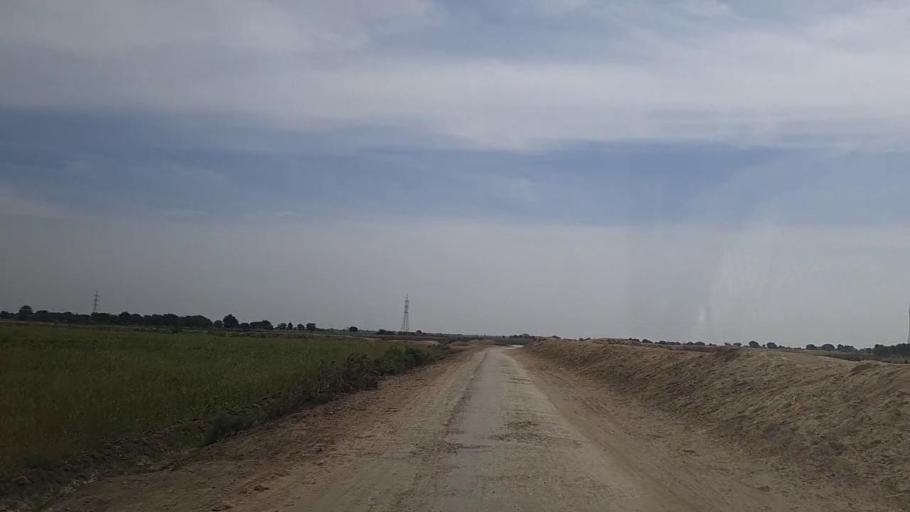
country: PK
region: Sindh
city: Samaro
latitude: 25.2965
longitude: 69.4533
